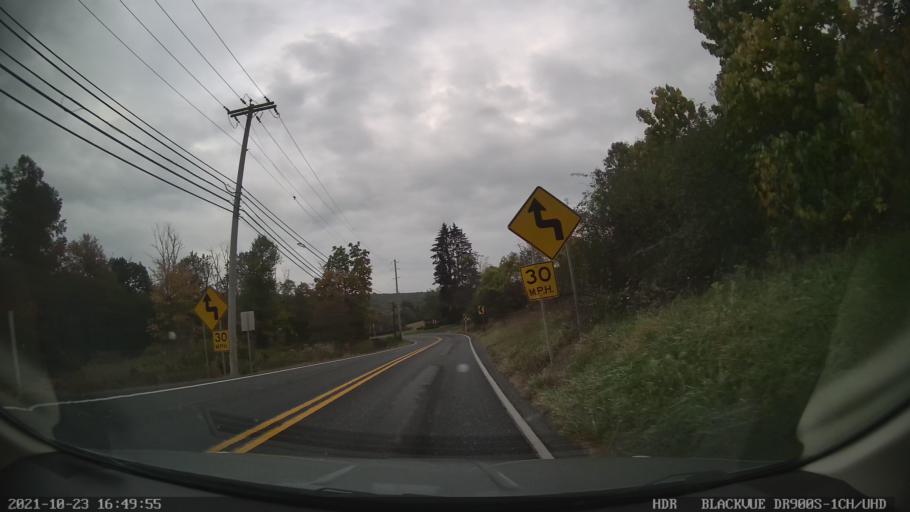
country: US
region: Pennsylvania
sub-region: Berks County
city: Red Lion
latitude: 40.4822
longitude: -75.6171
